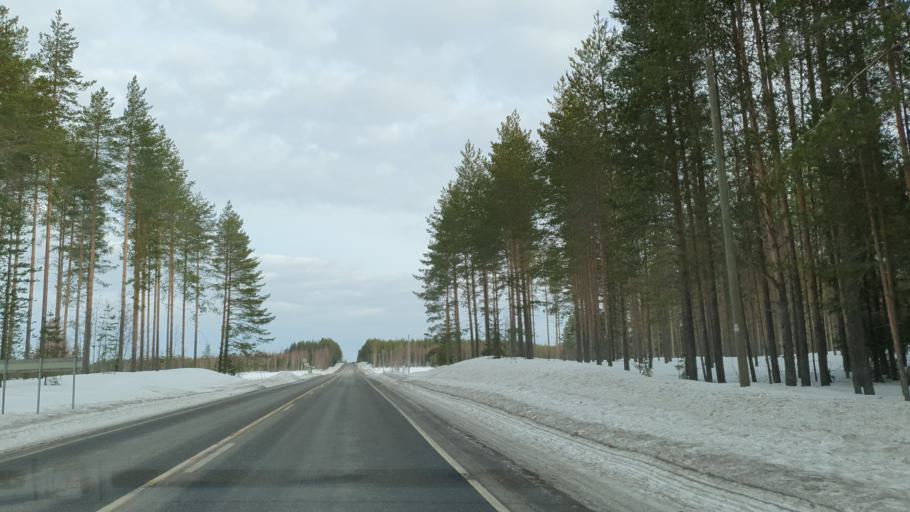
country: FI
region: Kainuu
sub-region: Kajaani
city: Vuokatti
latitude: 64.1808
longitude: 28.1915
